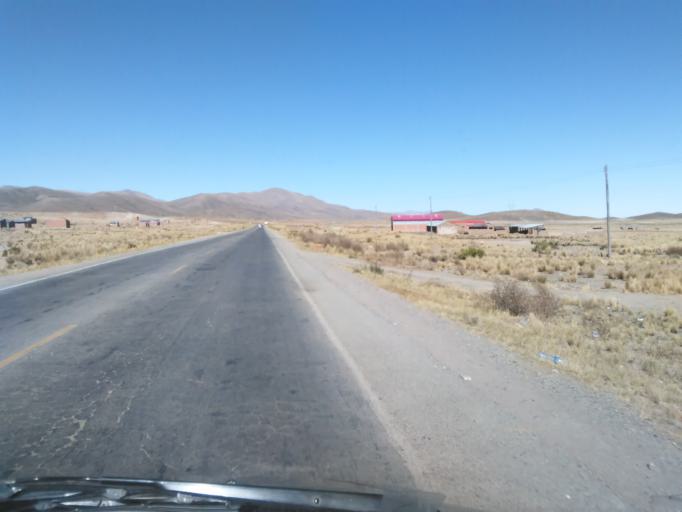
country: BO
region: Oruro
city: Oruro
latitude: -18.0256
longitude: -67.0250
